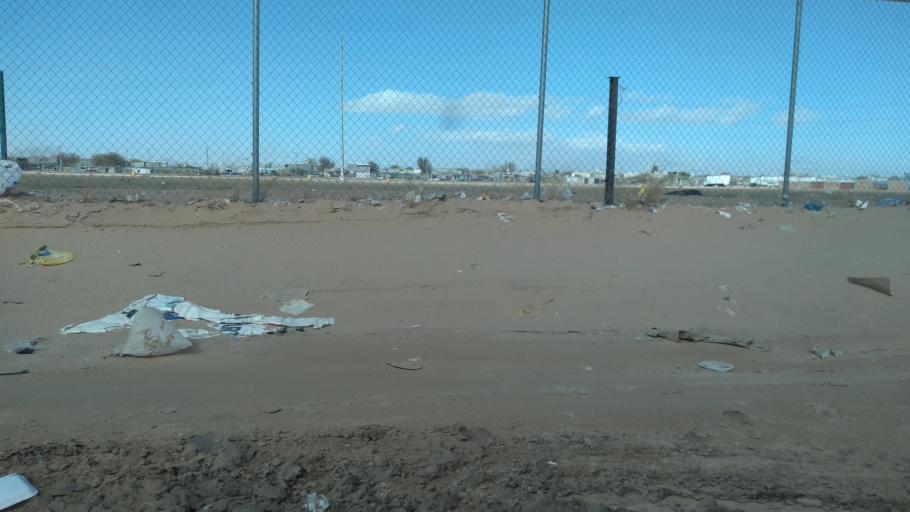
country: US
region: Texas
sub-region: El Paso County
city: Socorro Mission Number 1 Colonia
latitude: 31.5854
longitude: -106.3611
